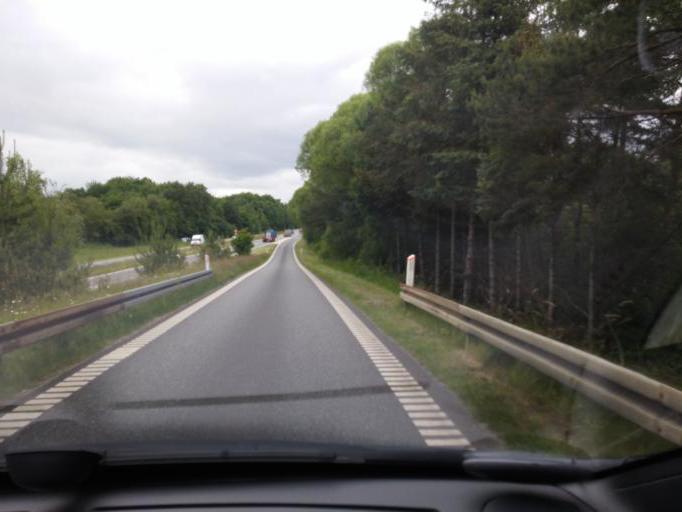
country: DK
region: Capital Region
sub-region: Hillerod Kommune
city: Nodebo
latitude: 55.9356
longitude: 12.3602
